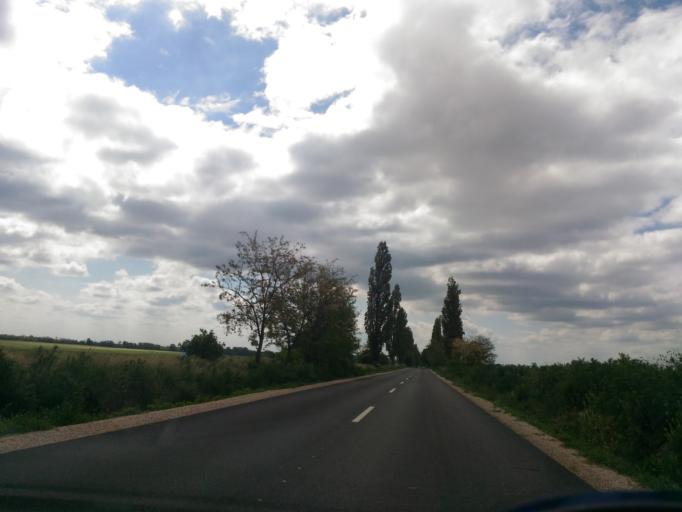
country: HU
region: Fejer
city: Pusztaszabolcs
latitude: 47.1813
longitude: 18.7161
